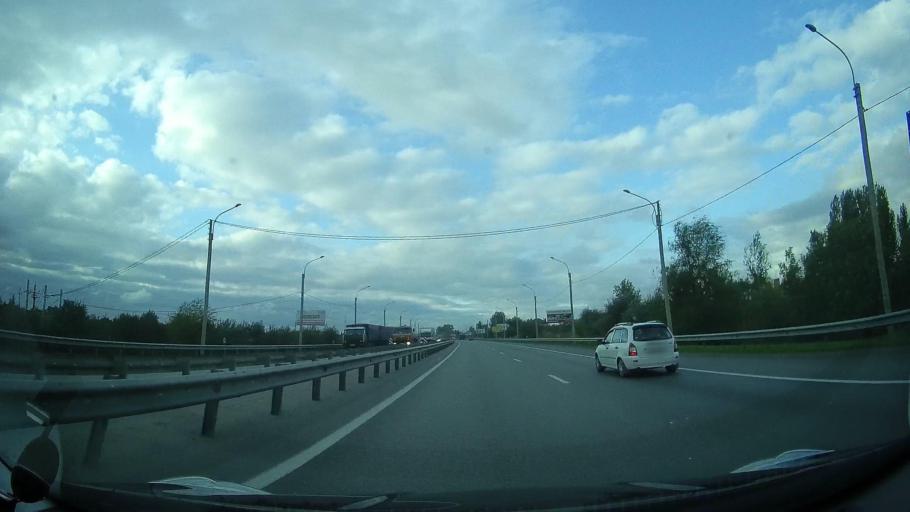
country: RU
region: Rostov
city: Bataysk
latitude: 47.1472
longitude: 39.7745
